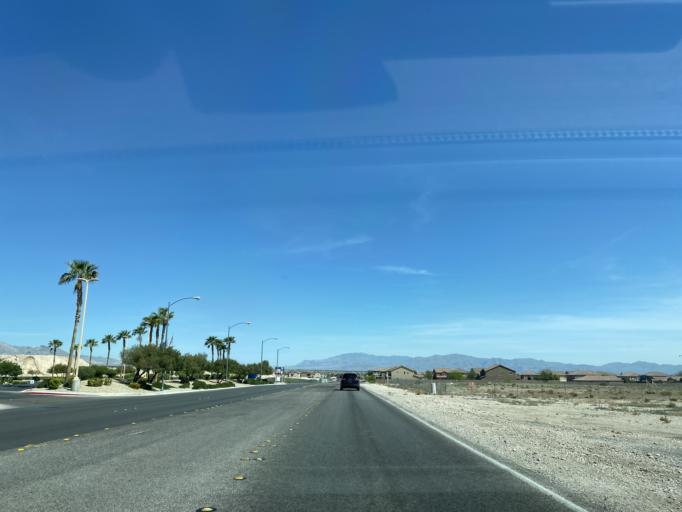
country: US
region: Nevada
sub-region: Clark County
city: Spring Valley
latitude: 36.0722
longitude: -115.2607
